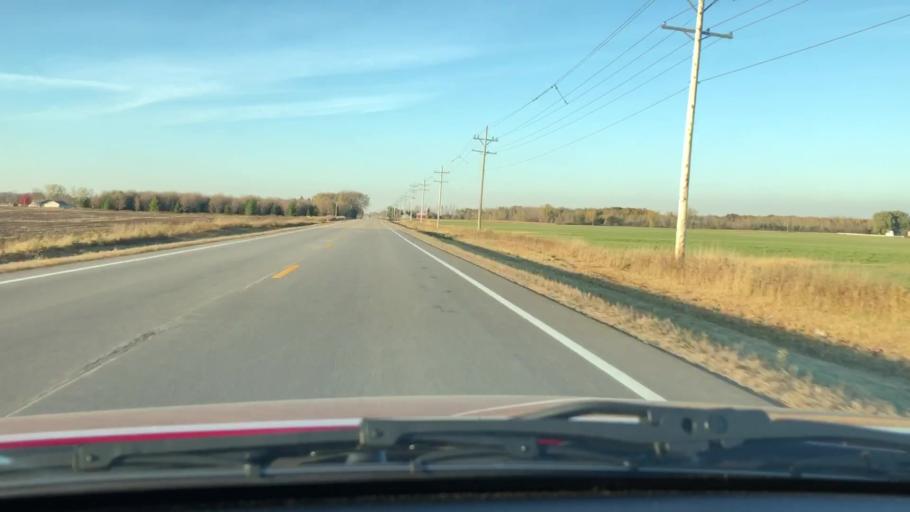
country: US
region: Wisconsin
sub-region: Outagamie County
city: Seymour
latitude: 44.4665
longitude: -88.2910
